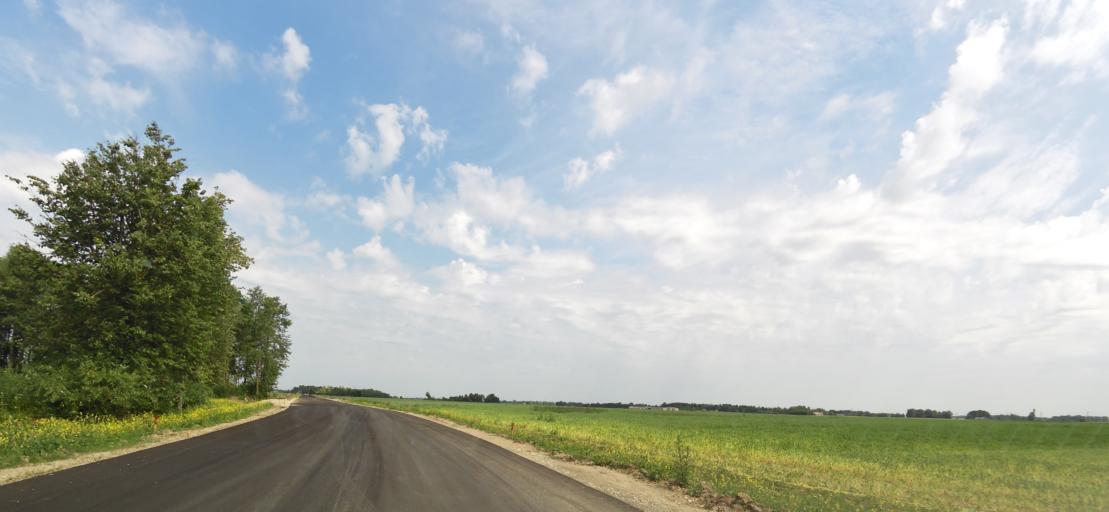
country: LT
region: Panevezys
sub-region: Birzai
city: Birzai
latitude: 56.2881
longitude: 24.6071
